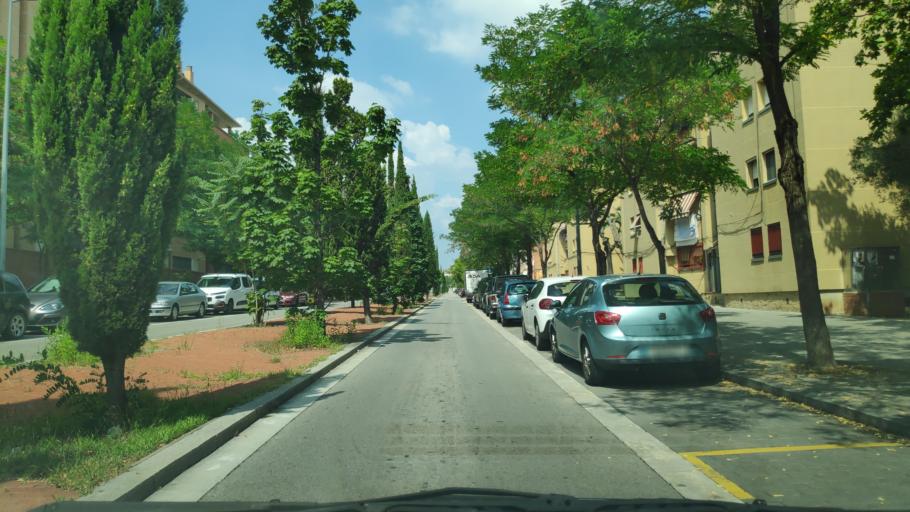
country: ES
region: Catalonia
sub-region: Provincia de Barcelona
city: Sant Quirze del Valles
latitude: 41.5437
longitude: 2.0869
